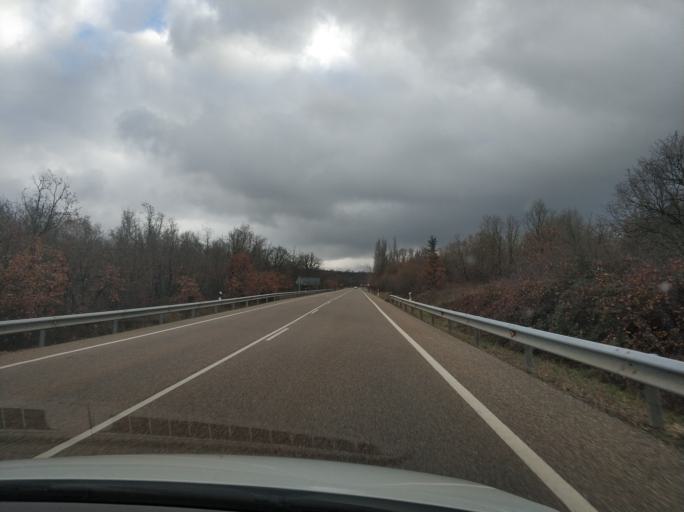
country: ES
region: Castille and Leon
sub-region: Provincia de Segovia
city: Riaza
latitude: 41.2996
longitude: -3.4773
